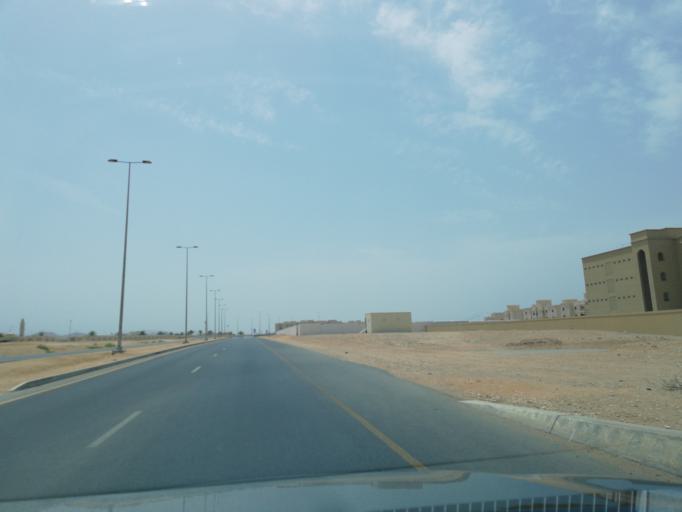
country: OM
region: Muhafazat Masqat
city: Bawshar
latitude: 23.5736
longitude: 58.2846
